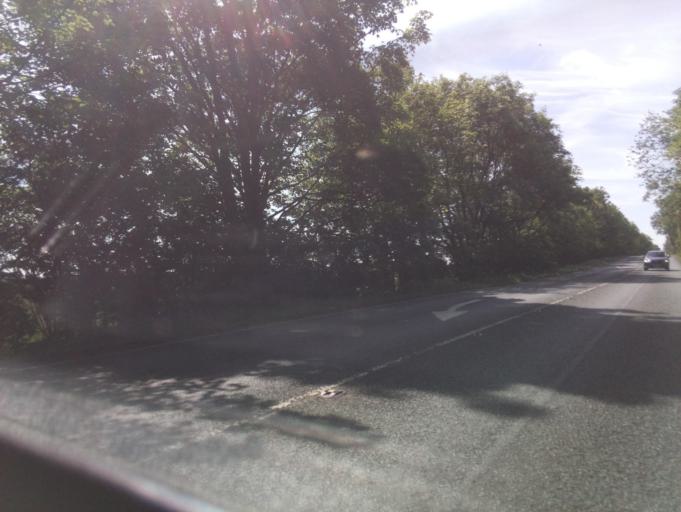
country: GB
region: England
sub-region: Lincolnshire
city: Burton
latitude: 53.3530
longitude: -0.5449
